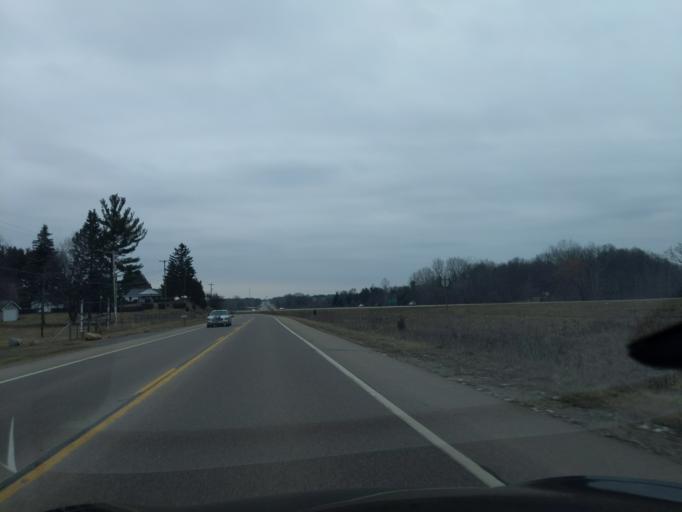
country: US
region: Michigan
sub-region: Eaton County
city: Dimondale
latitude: 42.6520
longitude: -84.6920
